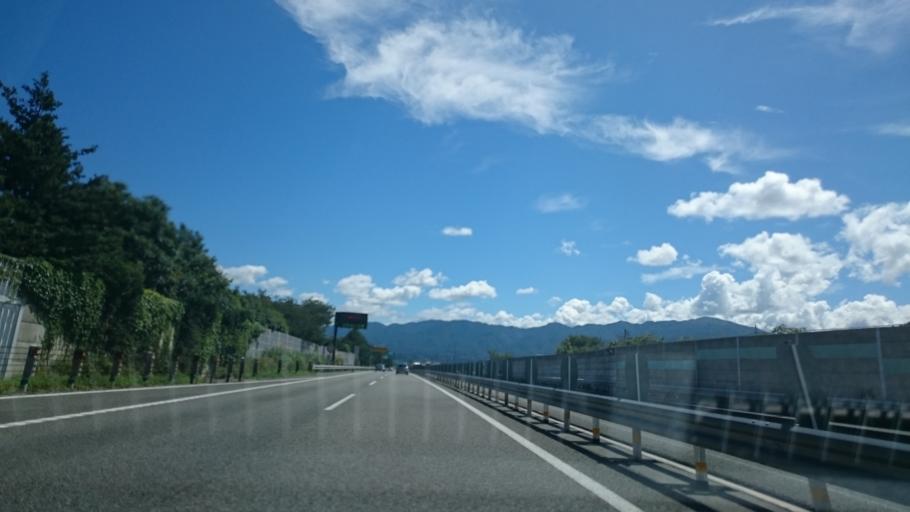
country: JP
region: Nagano
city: Iida
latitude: 35.4738
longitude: 137.7596
